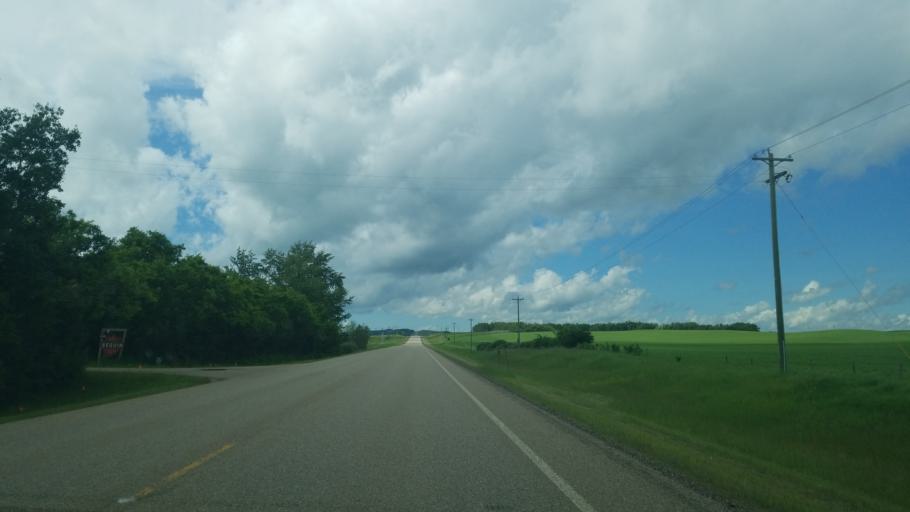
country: CA
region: Saskatchewan
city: Lloydminster
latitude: 53.1617
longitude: -110.1656
